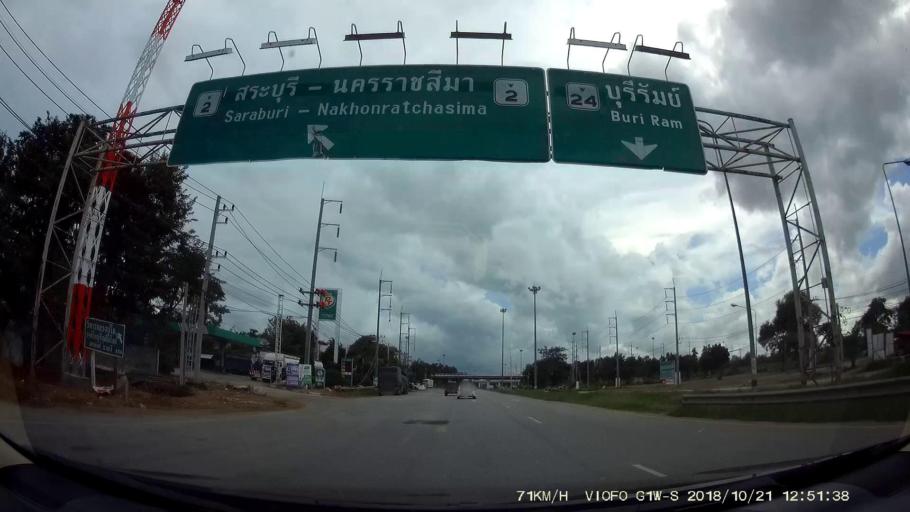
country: TH
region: Nakhon Ratchasima
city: Amphoe Sikhiu
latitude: 14.8665
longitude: 101.6968
